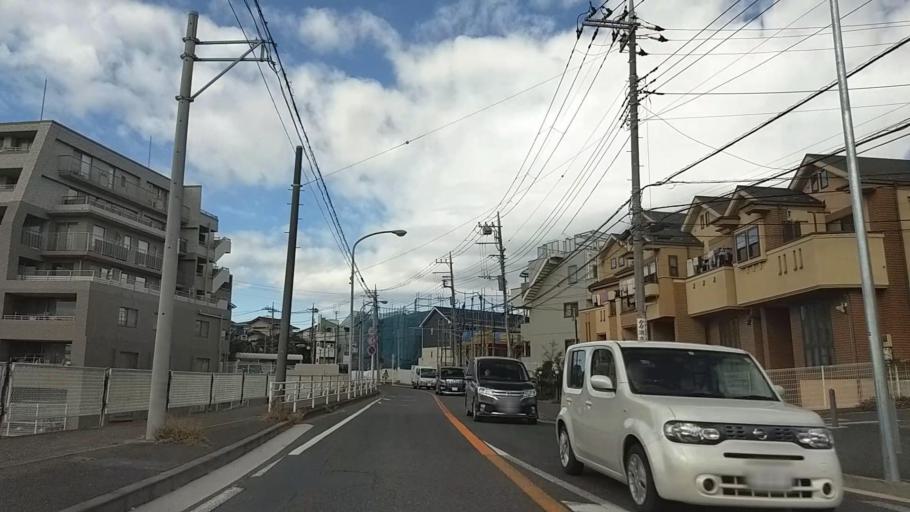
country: JP
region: Kanagawa
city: Yokohama
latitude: 35.5095
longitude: 139.6383
